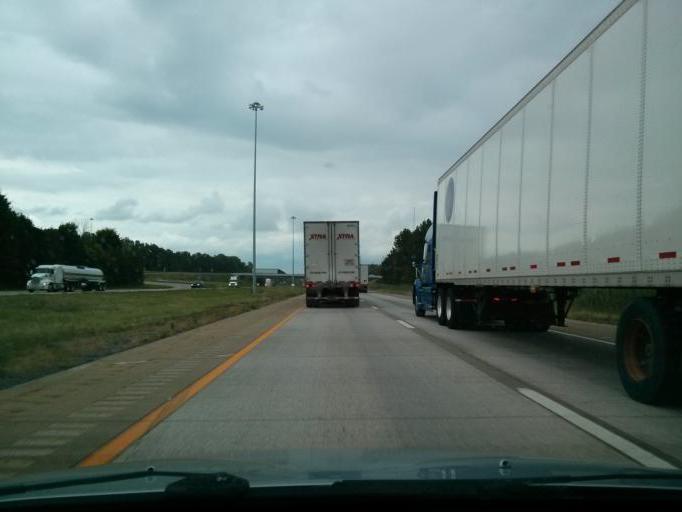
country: US
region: Ohio
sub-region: Trumbull County
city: Lordstown
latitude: 41.1098
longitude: -80.8375
